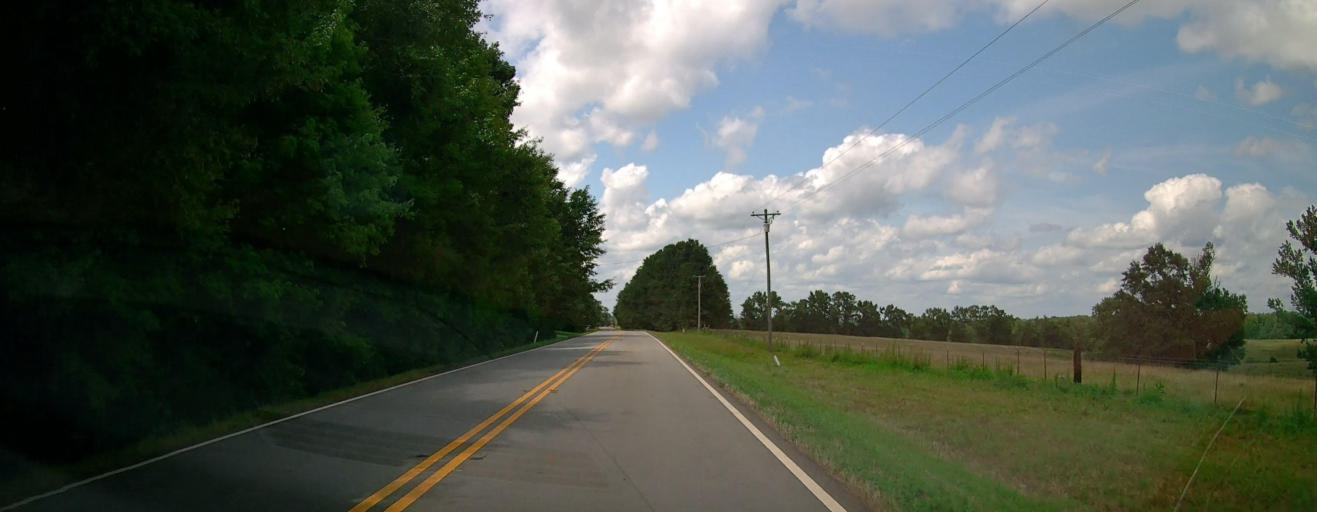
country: US
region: Georgia
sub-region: Carroll County
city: Bowdon
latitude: 33.4621
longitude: -85.2952
